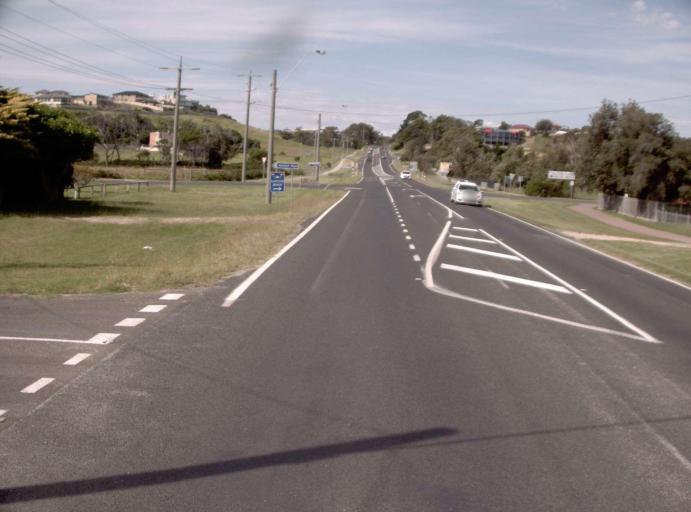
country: AU
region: Victoria
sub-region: East Gippsland
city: Lakes Entrance
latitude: -37.8737
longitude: 148.0085
